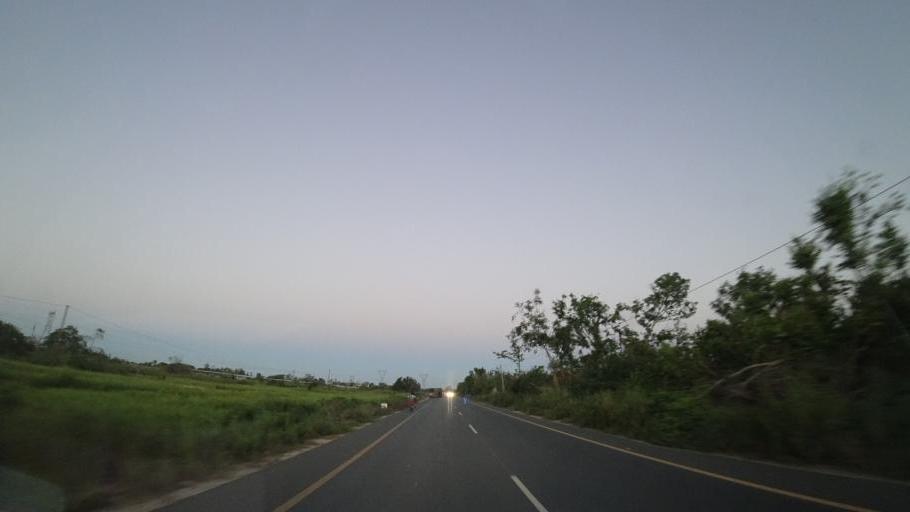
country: MZ
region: Sofala
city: Dondo
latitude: -19.5557
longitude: 34.6559
